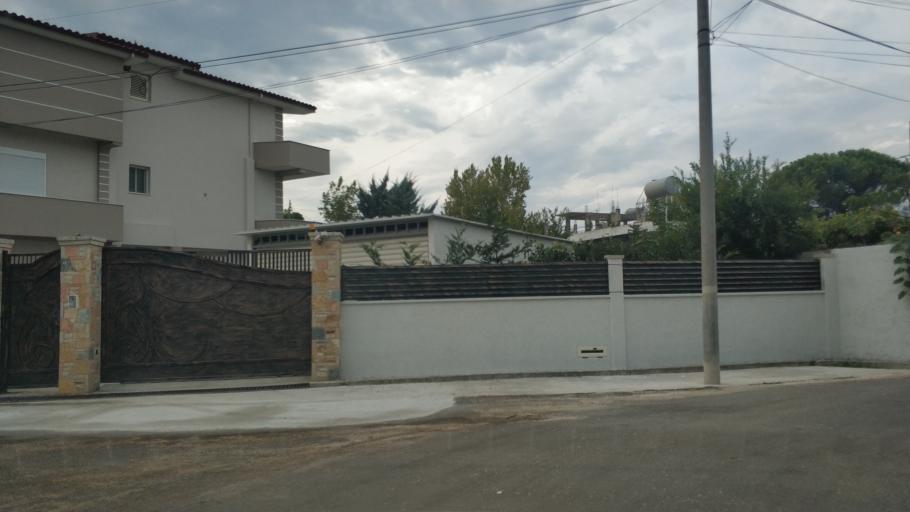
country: AL
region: Vlore
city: Vlore
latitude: 40.4619
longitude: 19.4684
